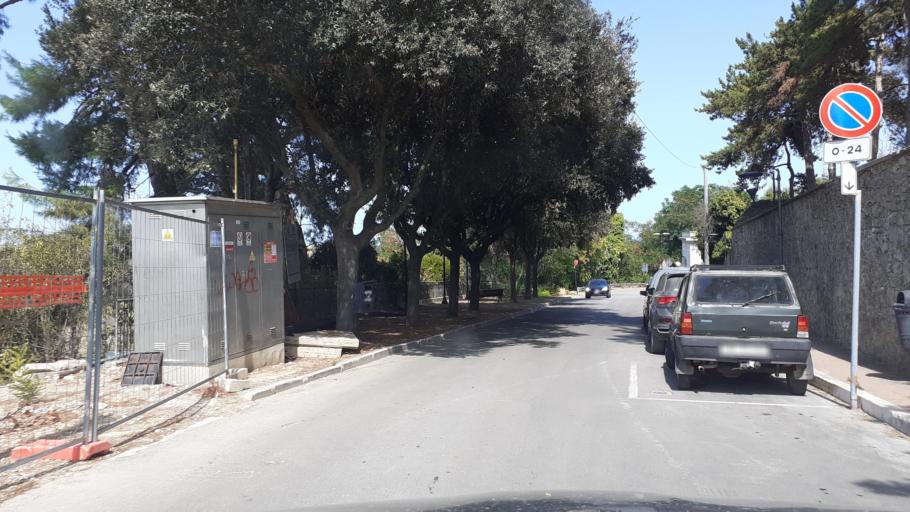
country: IT
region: Abruzzo
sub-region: Provincia di Chieti
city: Rocca San Giovanni
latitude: 42.2525
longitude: 14.4656
